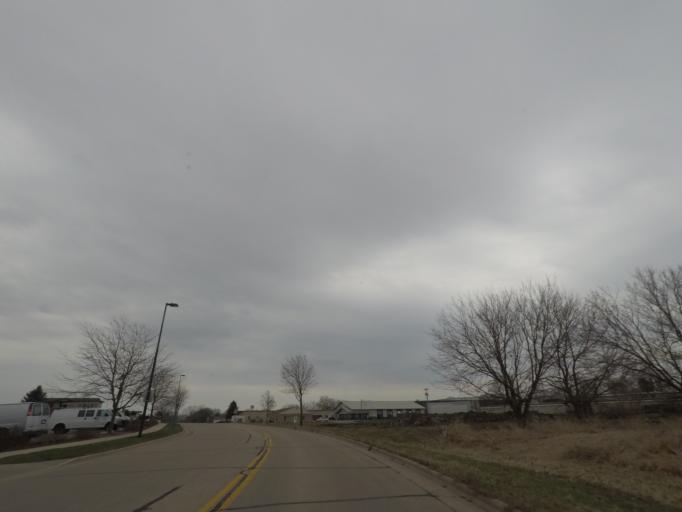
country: US
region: Wisconsin
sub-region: Dane County
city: Middleton
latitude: 43.1033
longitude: -89.5376
